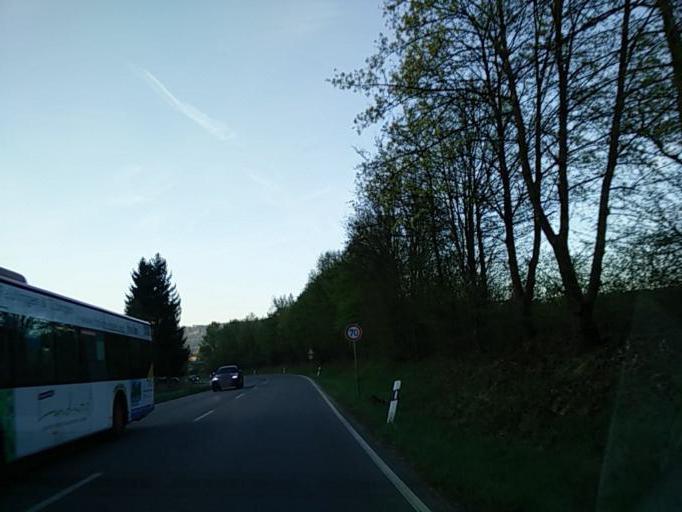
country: DE
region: Baden-Wuerttemberg
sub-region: Tuebingen Region
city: Tuebingen
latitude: 48.5283
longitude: 9.0234
